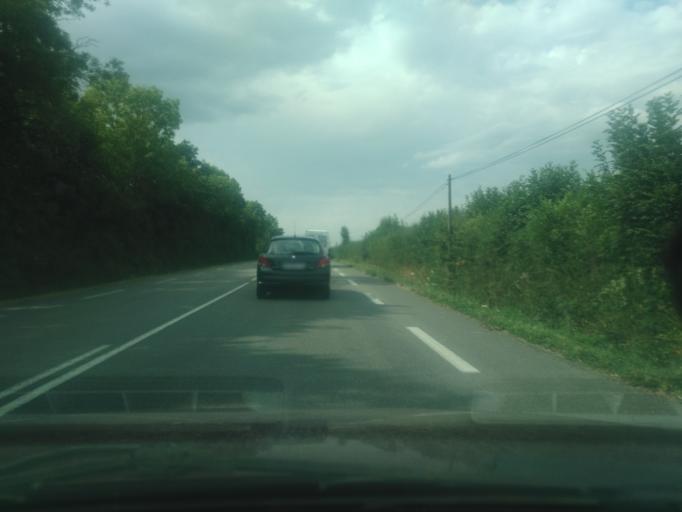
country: FR
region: Pays de la Loire
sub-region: Departement de la Vendee
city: Sainte-Cecile
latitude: 46.7770
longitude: -1.1146
